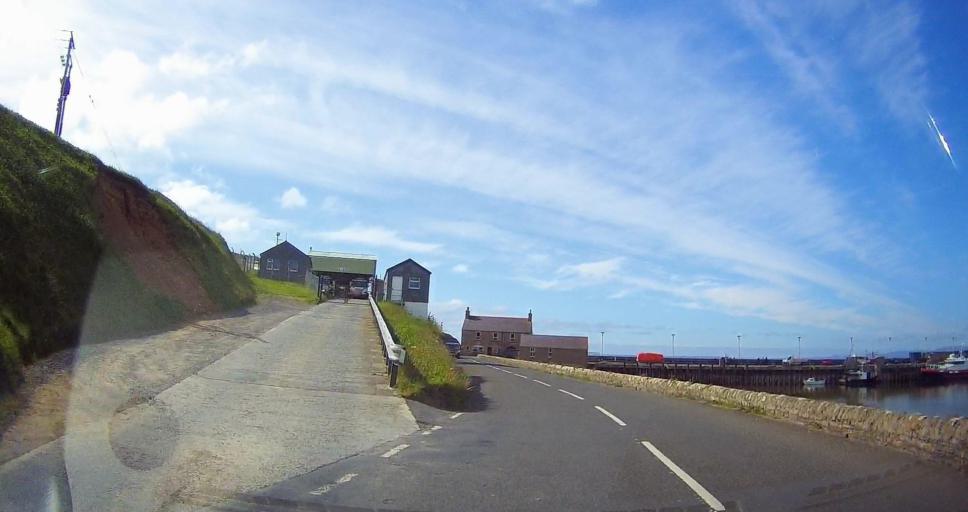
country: GB
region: Scotland
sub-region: Orkney Islands
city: Orkney
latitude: 58.9575
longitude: -2.9696
